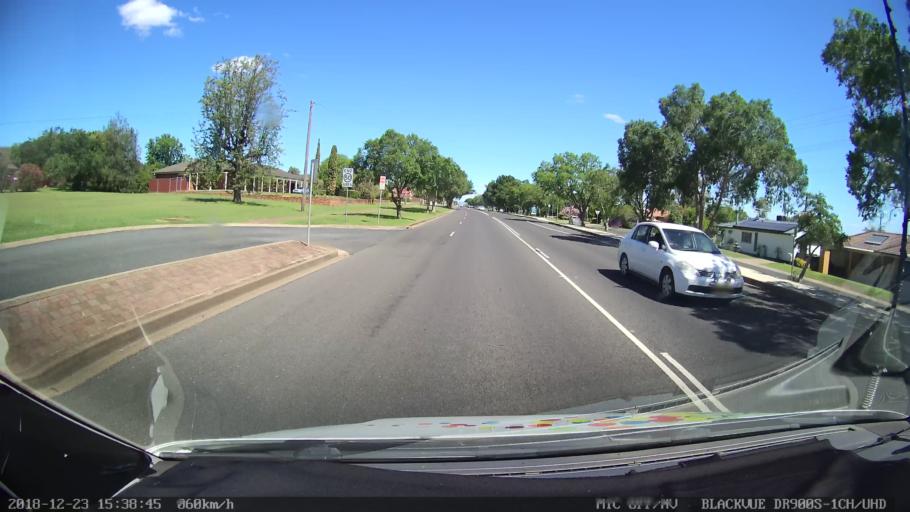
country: AU
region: New South Wales
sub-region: Tamworth Municipality
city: Tamworth
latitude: -31.0609
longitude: 150.8988
